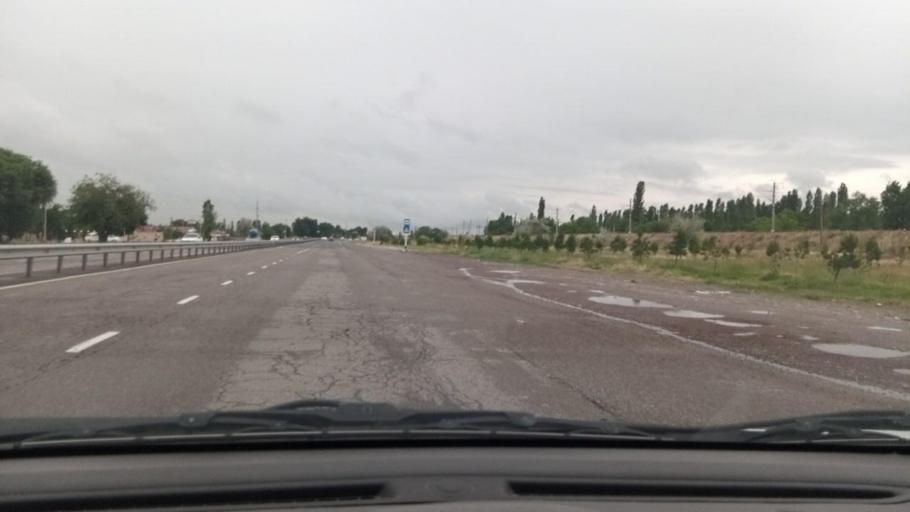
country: UZ
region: Toshkent
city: Ohangaron
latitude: 40.9083
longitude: 69.8025
